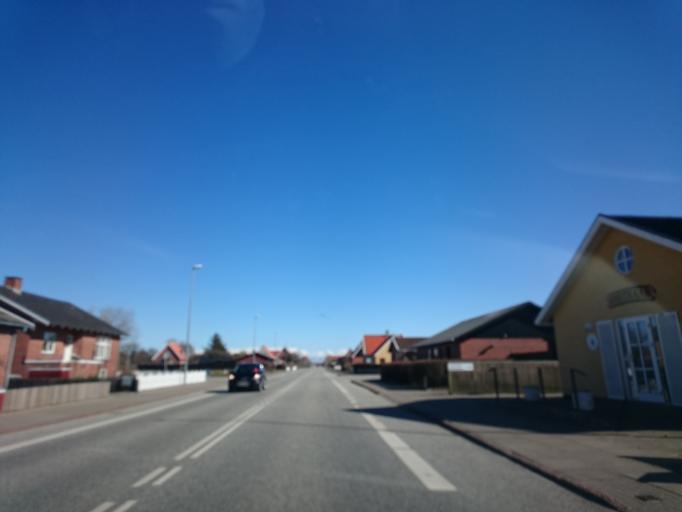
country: DK
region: North Denmark
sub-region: Frederikshavn Kommune
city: Skagen
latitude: 57.7271
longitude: 10.5790
